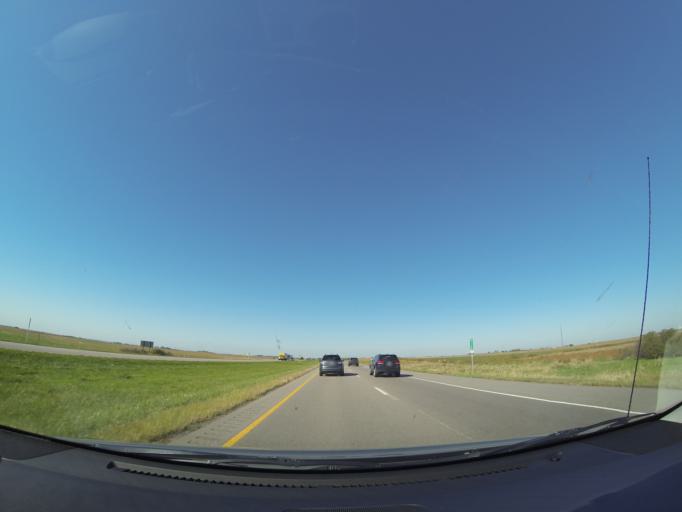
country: US
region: Nebraska
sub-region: Saline County
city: Friend
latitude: 40.8219
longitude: -97.3094
